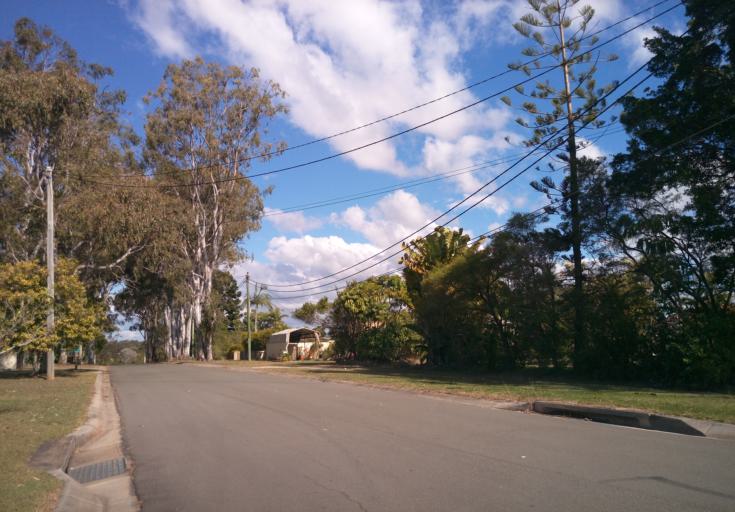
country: AU
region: Queensland
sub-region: Redland
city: Wellington Point
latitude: -27.4906
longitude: 153.2099
